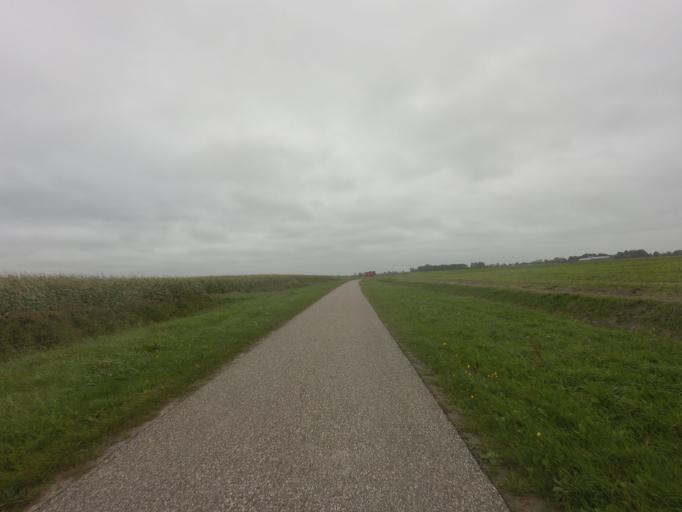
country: NL
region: Friesland
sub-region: Gemeente Ferwerderadiel
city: Ferwert
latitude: 53.3459
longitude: 5.8572
